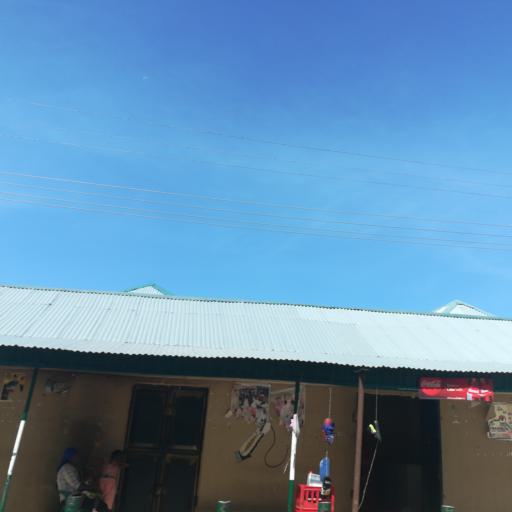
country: NG
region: Plateau
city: Bukuru
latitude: 9.7605
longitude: 8.8801
